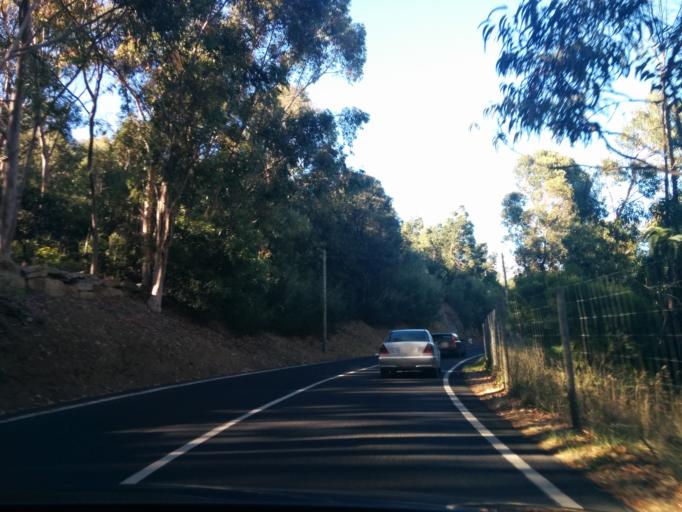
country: PT
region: Lisbon
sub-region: Cascais
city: Alcabideche
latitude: 38.7474
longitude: -9.4514
